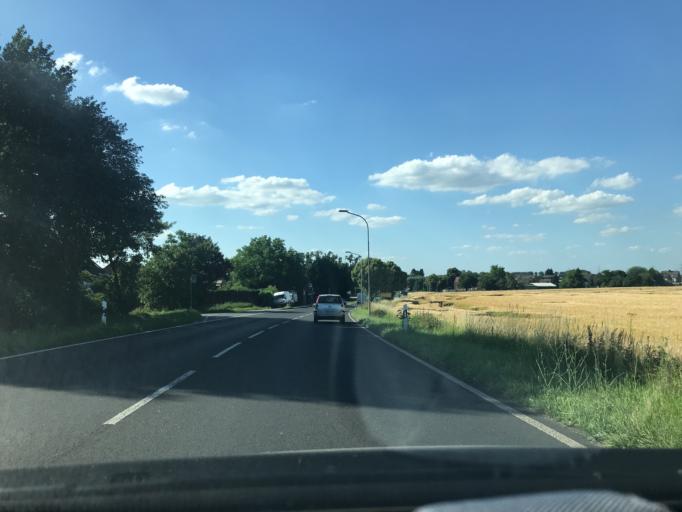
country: DE
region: North Rhine-Westphalia
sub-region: Regierungsbezirk Dusseldorf
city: Neubrueck
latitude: 51.1352
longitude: 6.6804
